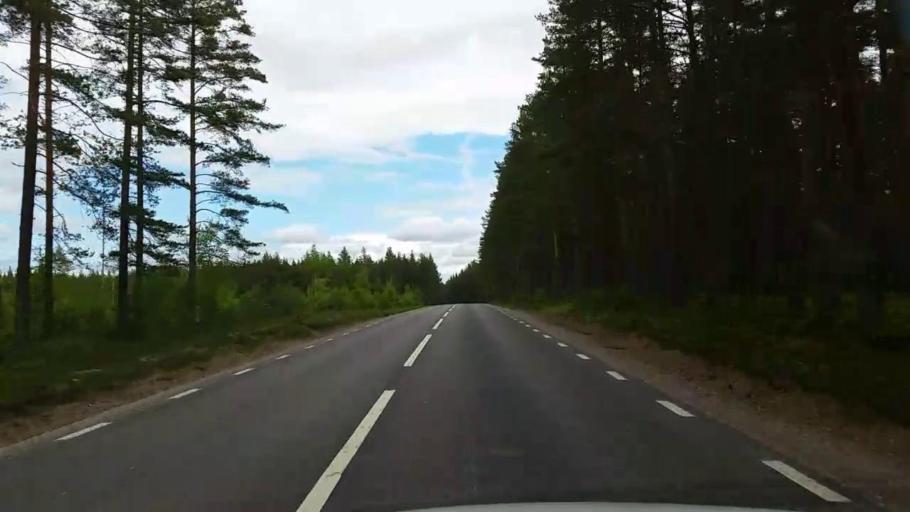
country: SE
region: Gaevleborg
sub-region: Sandvikens Kommun
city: Jarbo
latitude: 60.9523
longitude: 16.3980
